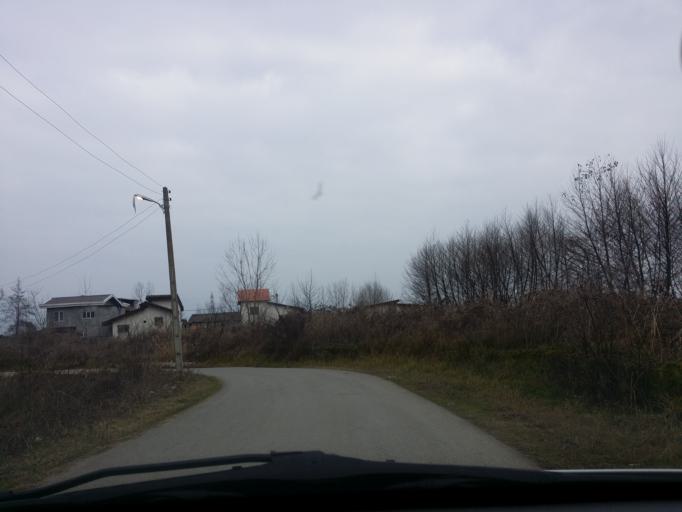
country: IR
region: Mazandaran
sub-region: Nowshahr
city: Nowshahr
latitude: 36.6498
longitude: 51.4719
